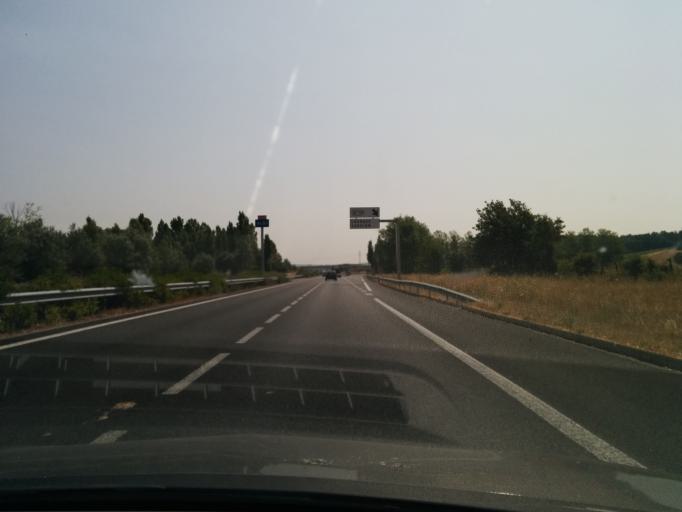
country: FR
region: Midi-Pyrenees
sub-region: Departement du Tarn
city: Lagrave
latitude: 43.8891
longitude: 1.9609
